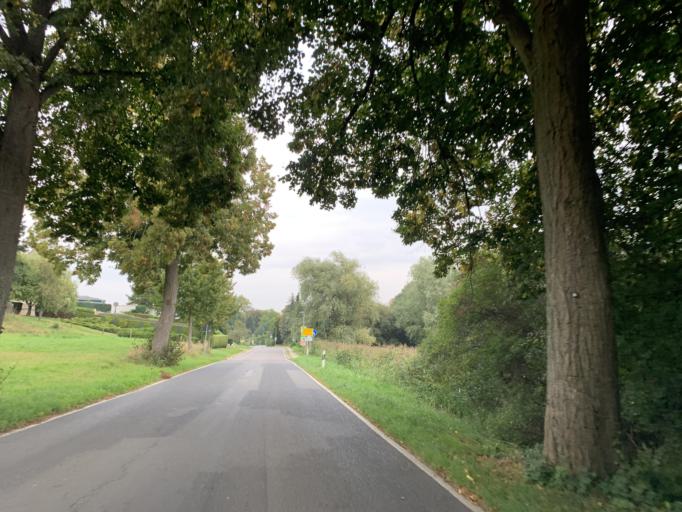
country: DE
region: Mecklenburg-Vorpommern
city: Woldegk
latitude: 53.3354
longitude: 13.4990
